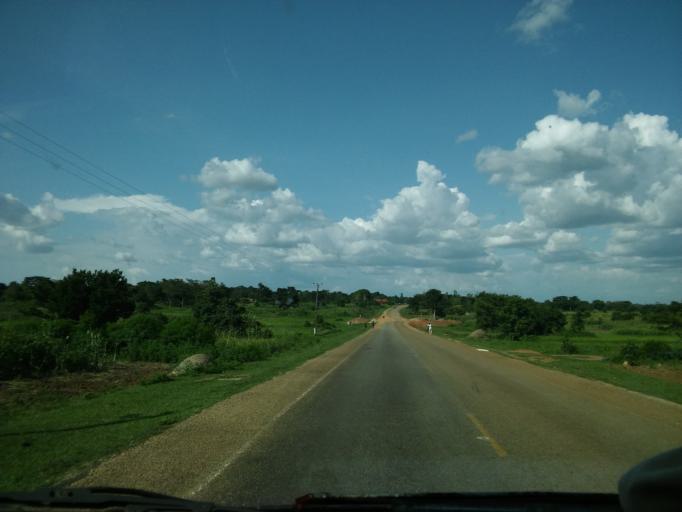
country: UG
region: Eastern Region
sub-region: Kibuku District
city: Kibuku
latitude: 1.0111
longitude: 33.7980
